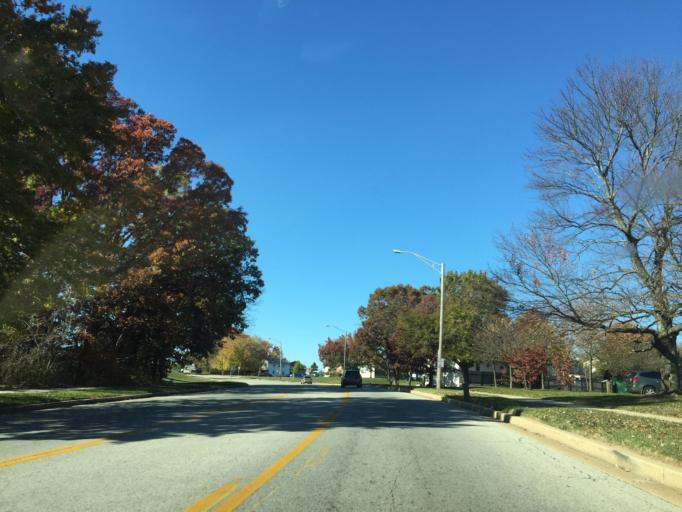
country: US
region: Maryland
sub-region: Baltimore County
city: Lansdowne
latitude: 39.2505
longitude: -76.6549
